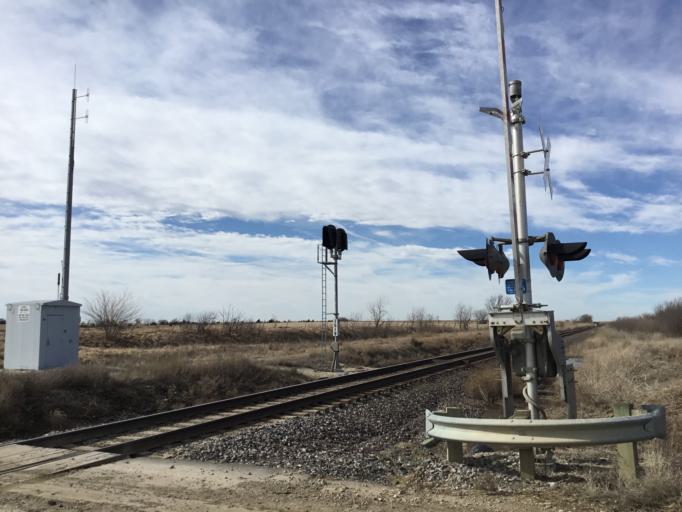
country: US
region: Kansas
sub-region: Geary County
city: Grandview Plaza
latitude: 38.8297
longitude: -96.6680
